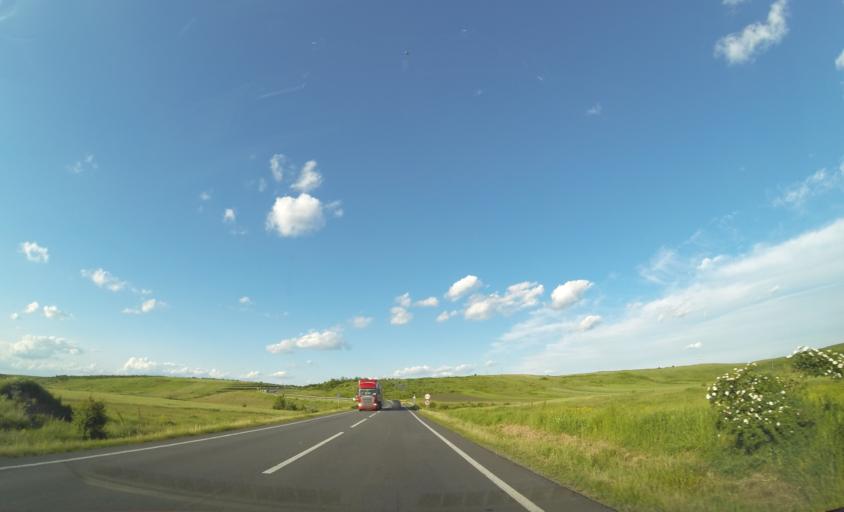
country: RO
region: Dolj
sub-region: Comuna Pielesti
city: Pielesti
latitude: 44.3322
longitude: 23.9926
